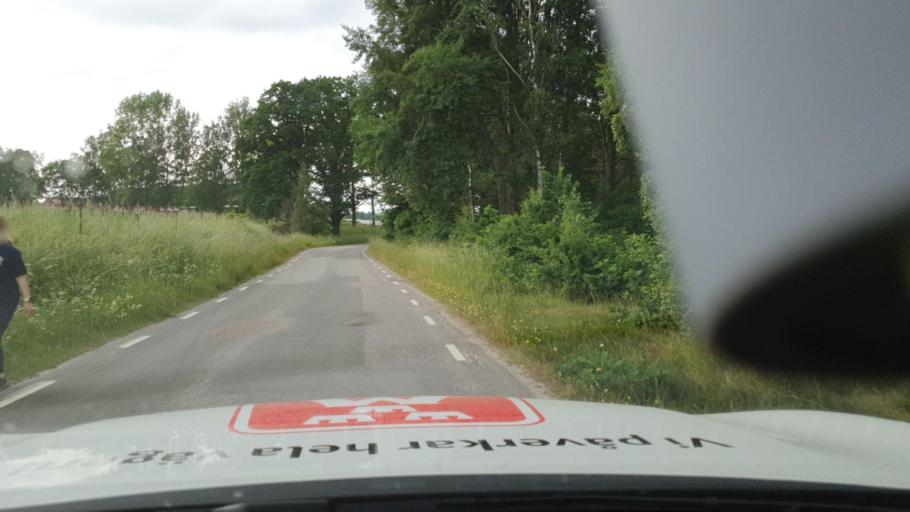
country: SE
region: Vaestra Goetaland
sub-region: Hjo Kommun
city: Hjo
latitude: 58.1695
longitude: 14.2015
